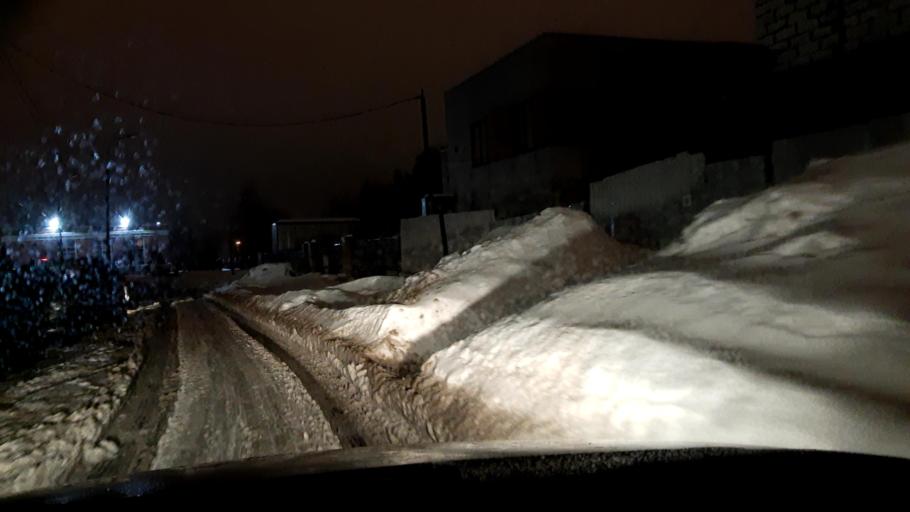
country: RU
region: Moscow
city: Novo-Peredelkino
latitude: 55.6526
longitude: 37.3484
